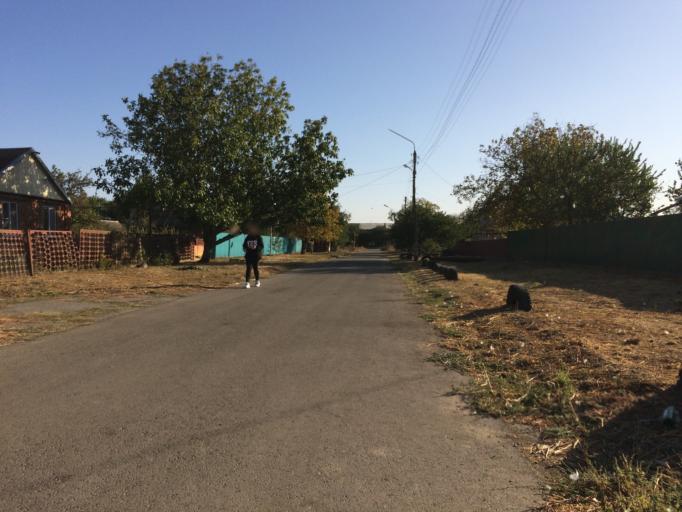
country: RU
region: Rostov
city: Tselina
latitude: 46.5177
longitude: 41.1859
